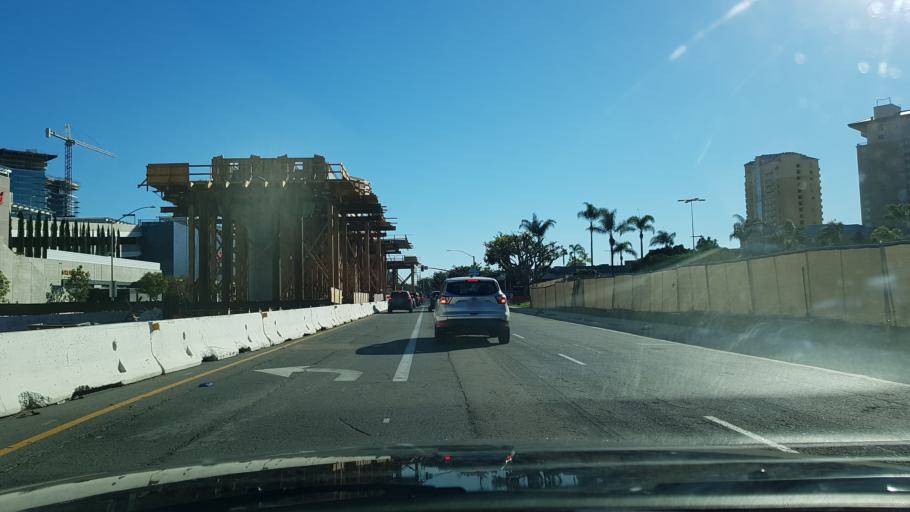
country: US
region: California
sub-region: San Diego County
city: La Jolla
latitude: 32.8710
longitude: -117.2142
